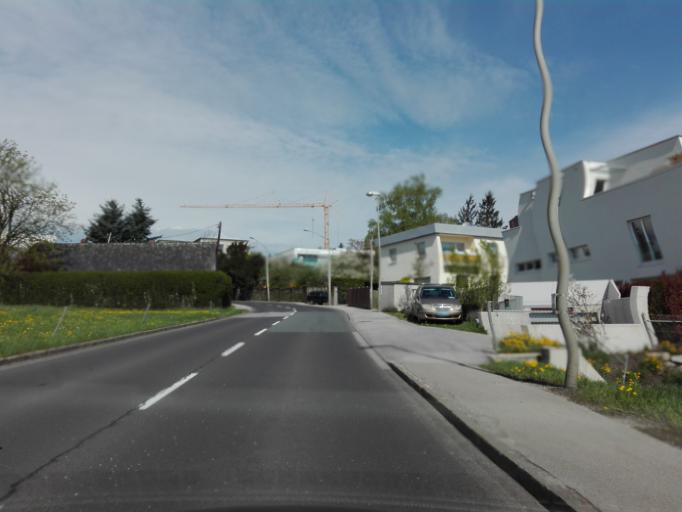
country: AT
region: Upper Austria
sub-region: Linz Stadt
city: Linz
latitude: 48.3122
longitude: 14.2623
